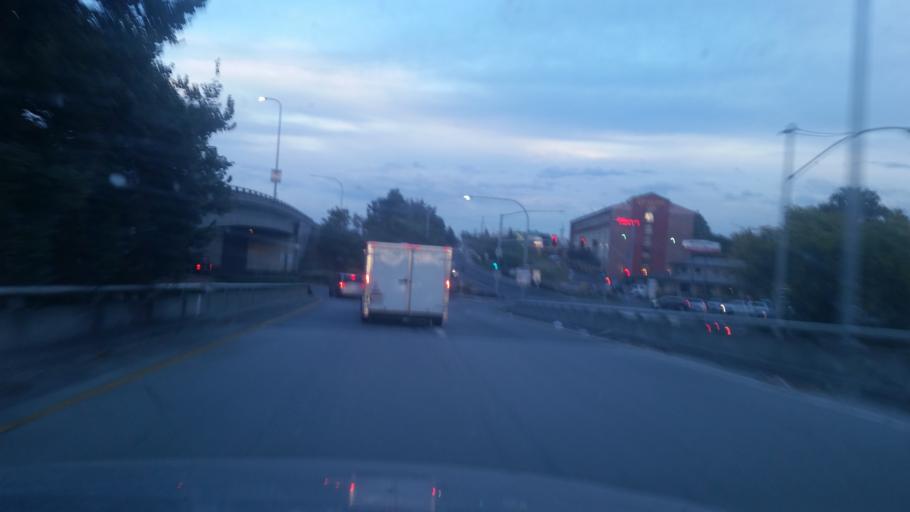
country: US
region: Washington
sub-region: Spokane County
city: Spokane
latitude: 47.6529
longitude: -117.4123
